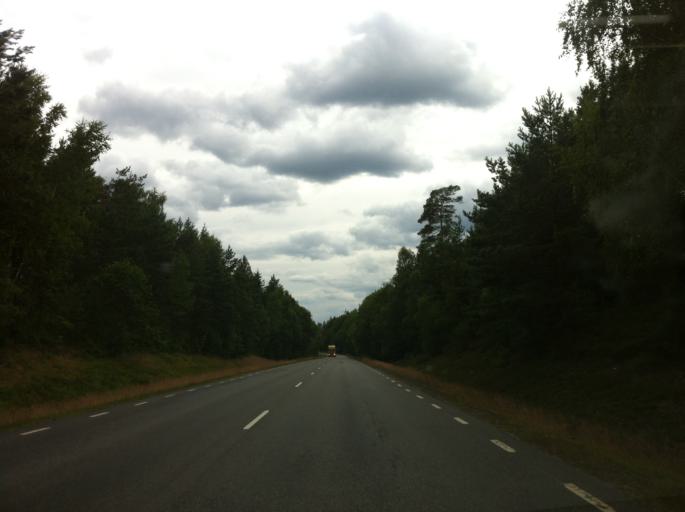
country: SE
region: Skane
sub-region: Osby Kommun
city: Lonsboda
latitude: 56.3808
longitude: 14.2641
